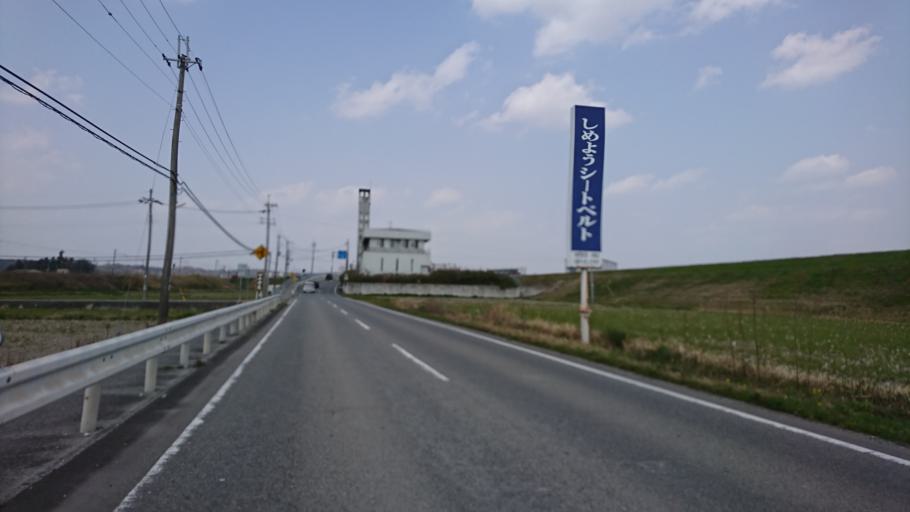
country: JP
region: Hyogo
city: Ono
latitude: 34.8491
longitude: 134.9098
